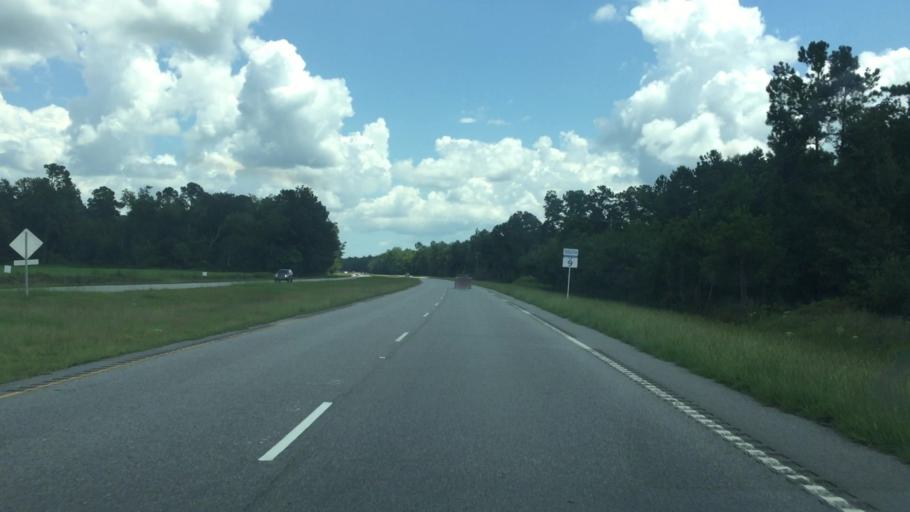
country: US
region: South Carolina
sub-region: Horry County
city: Loris
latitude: 34.0481
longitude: -78.8344
